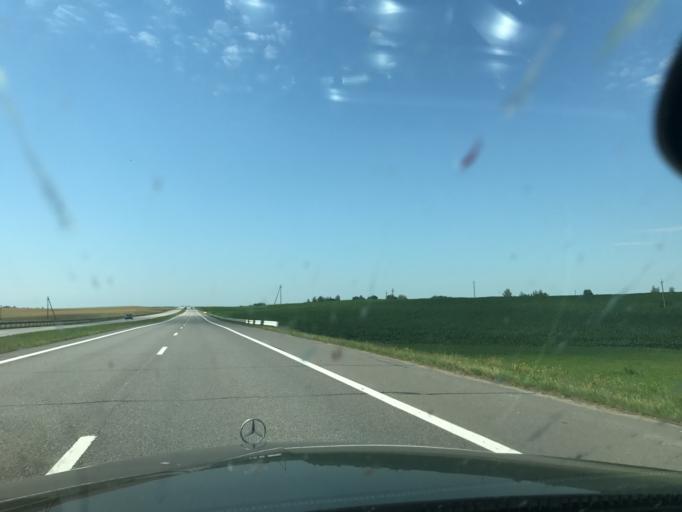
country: BY
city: Fanipol
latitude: 53.6896
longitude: 27.3453
